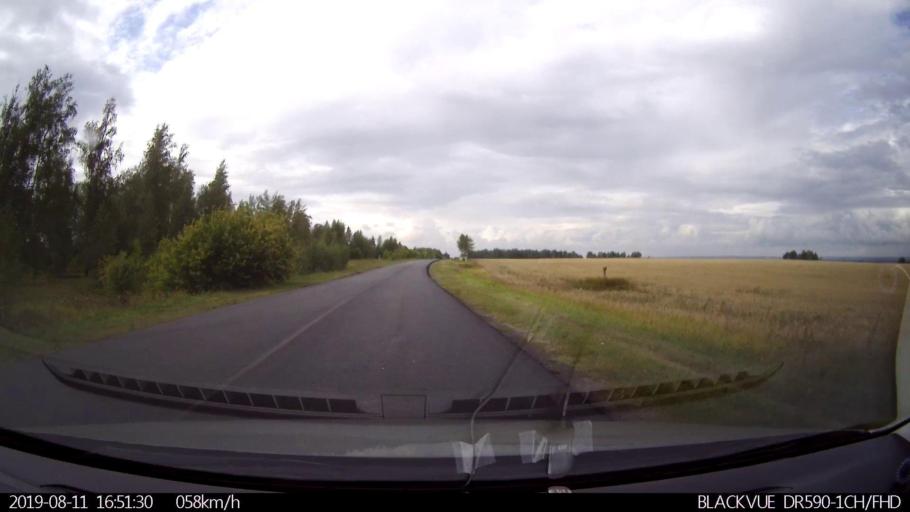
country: RU
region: Ulyanovsk
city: Mayna
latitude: 54.2378
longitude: 47.6768
